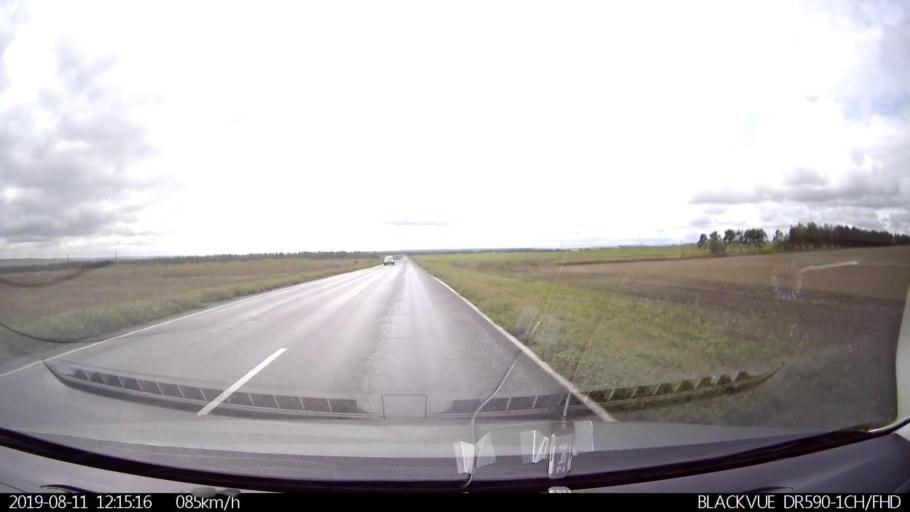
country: RU
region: Ulyanovsk
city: Ignatovka
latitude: 53.9435
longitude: 47.9701
